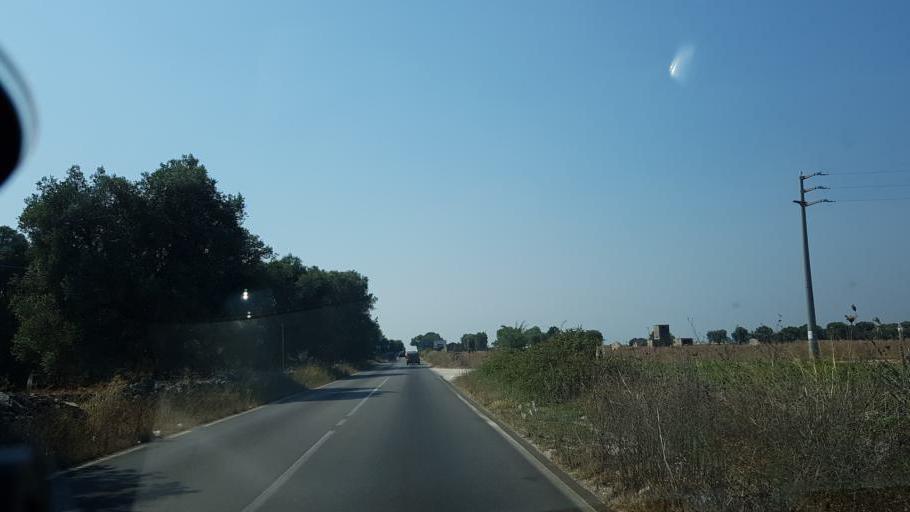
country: IT
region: Apulia
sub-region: Provincia di Brindisi
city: Oria
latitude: 40.4527
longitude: 17.6374
